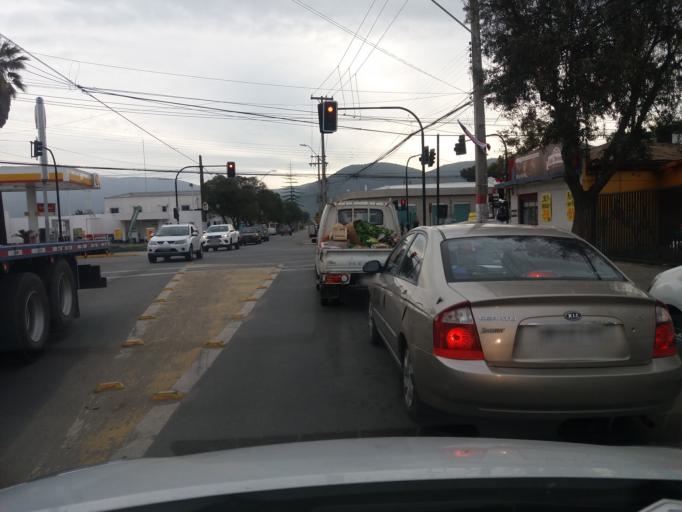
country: CL
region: Valparaiso
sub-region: Provincia de Quillota
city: Hacienda La Calera
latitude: -32.7777
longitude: -71.1912
